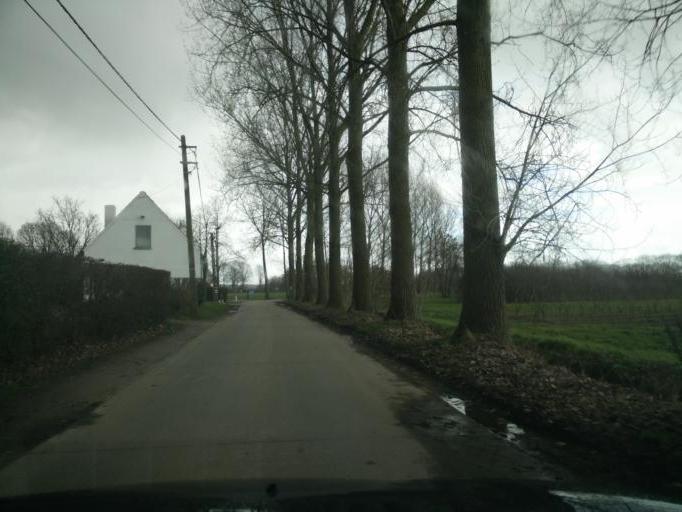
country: BE
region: Flanders
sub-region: Provincie Oost-Vlaanderen
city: Laarne
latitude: 51.0477
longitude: 3.8375
